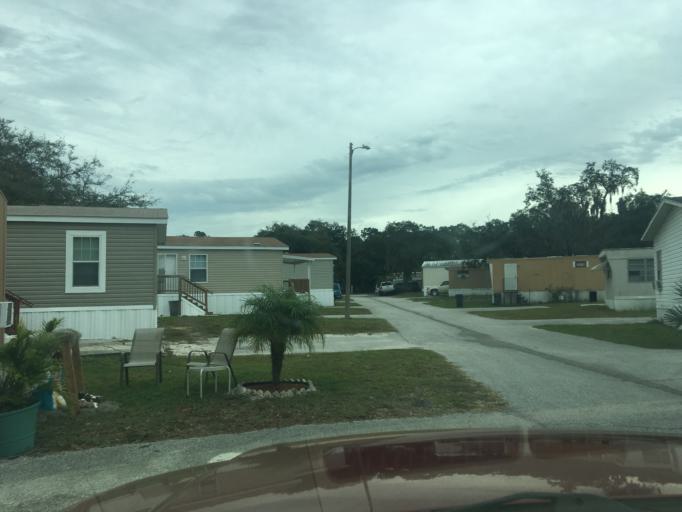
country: US
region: Florida
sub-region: Hillsborough County
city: Gibsonton
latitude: 27.8512
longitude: -82.3595
